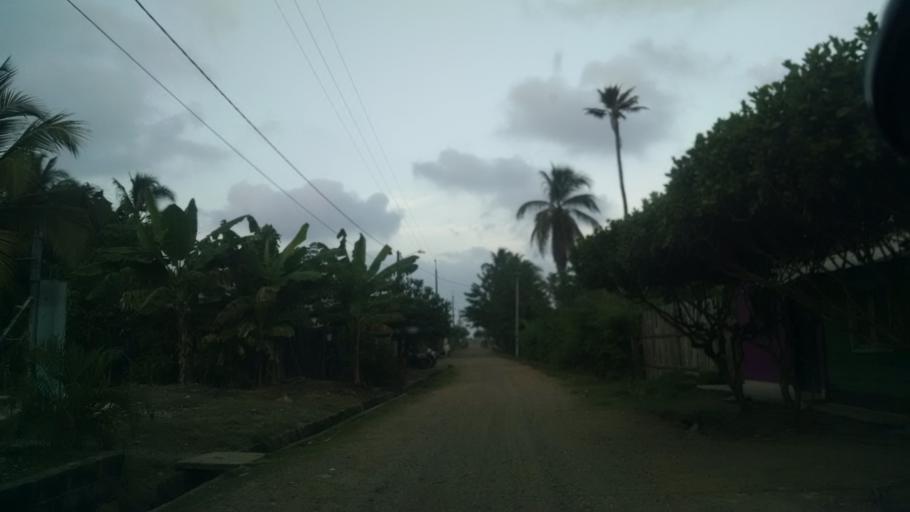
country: CO
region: Antioquia
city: San Juan de Uraba
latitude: 8.7382
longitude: -76.6066
